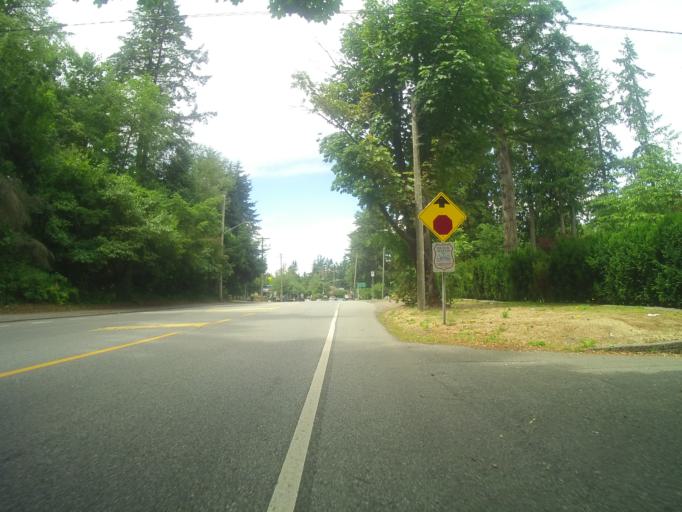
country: CA
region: British Columbia
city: Surrey
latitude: 49.0533
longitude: -122.8657
